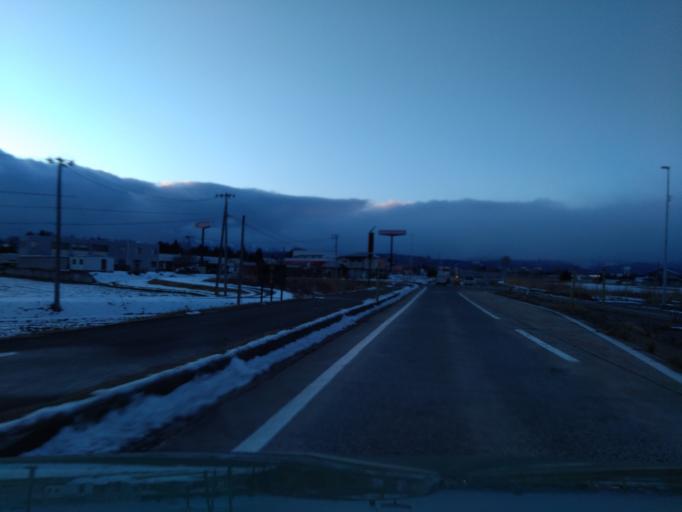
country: JP
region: Iwate
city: Shizukuishi
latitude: 39.6920
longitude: 140.9841
